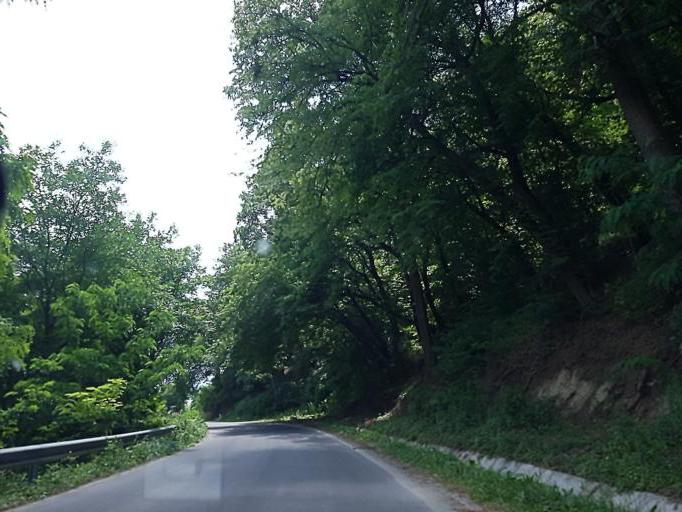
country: RO
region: Sibiu
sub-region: Comuna Seica Mare
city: Seica Mare
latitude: 46.0379
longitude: 24.1602
